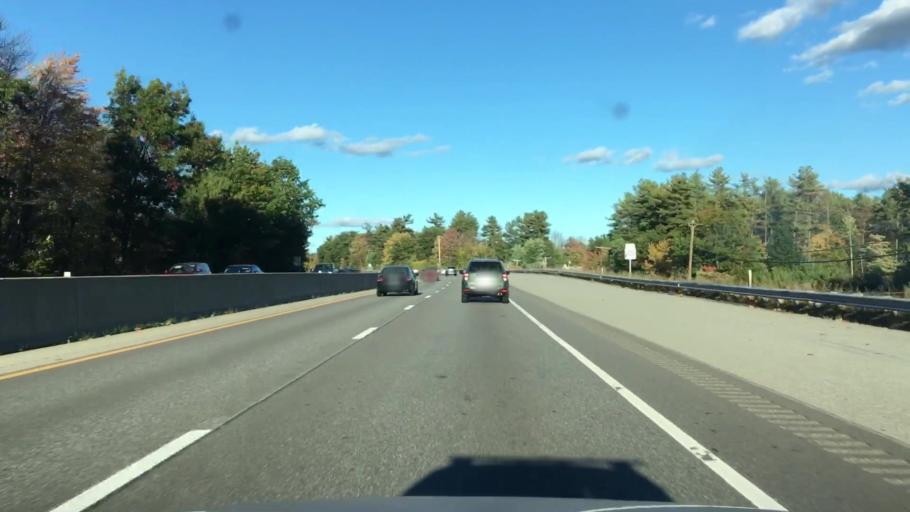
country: US
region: New Hampshire
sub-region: Rockingham County
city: Auburn
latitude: 43.0095
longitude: -71.3867
